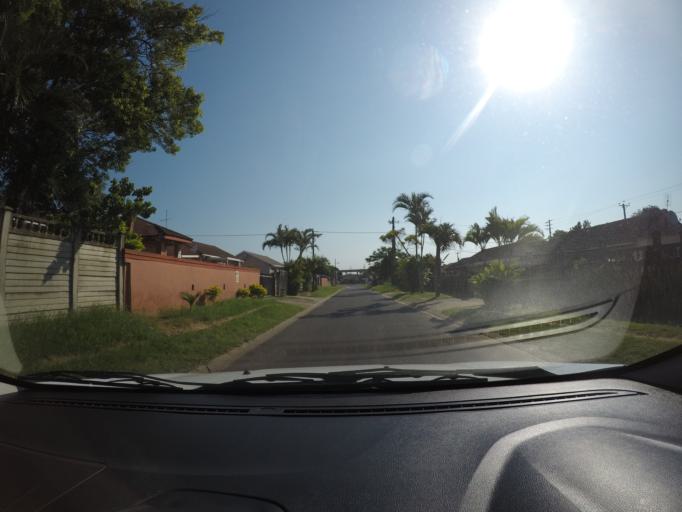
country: ZA
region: KwaZulu-Natal
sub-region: uThungulu District Municipality
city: Richards Bay
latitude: -28.7179
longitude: 32.0401
